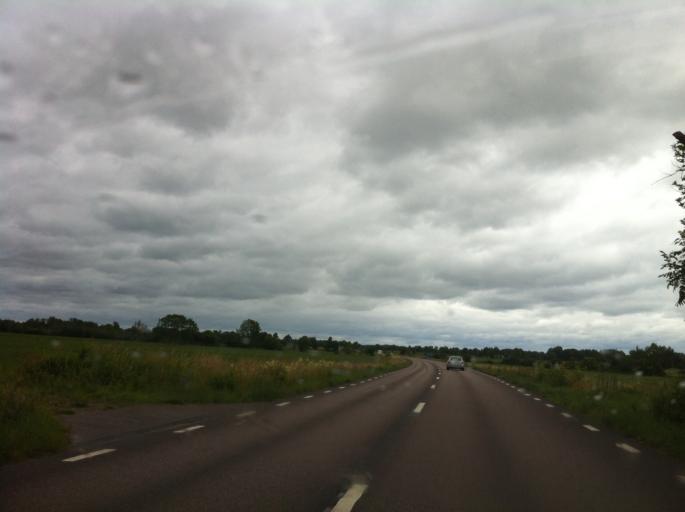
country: SE
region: Kalmar
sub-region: Borgholms Kommun
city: Borgholm
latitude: 57.1220
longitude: 16.9657
